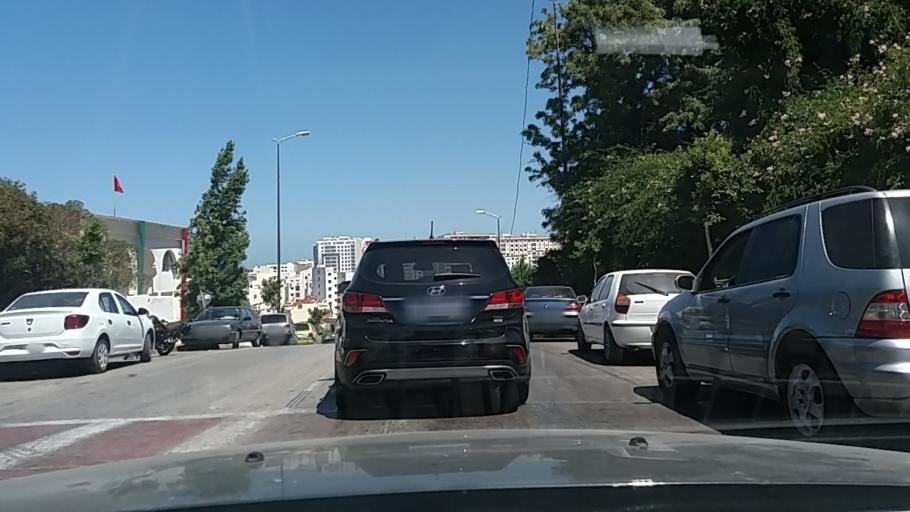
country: MA
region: Tanger-Tetouan
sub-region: Tanger-Assilah
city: Tangier
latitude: 35.7674
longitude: -5.7936
